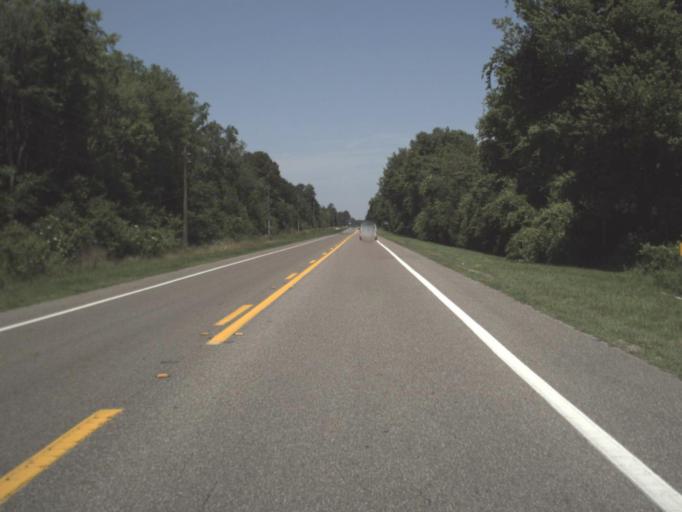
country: US
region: Florida
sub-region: Suwannee County
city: Wellborn
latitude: 30.2418
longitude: -82.8630
